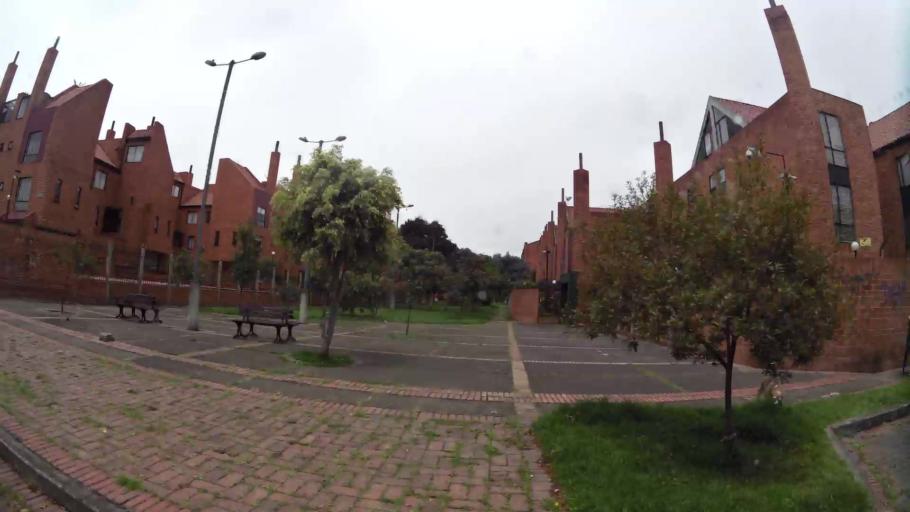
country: CO
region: Bogota D.C.
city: Bogota
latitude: 4.6492
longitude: -74.1105
